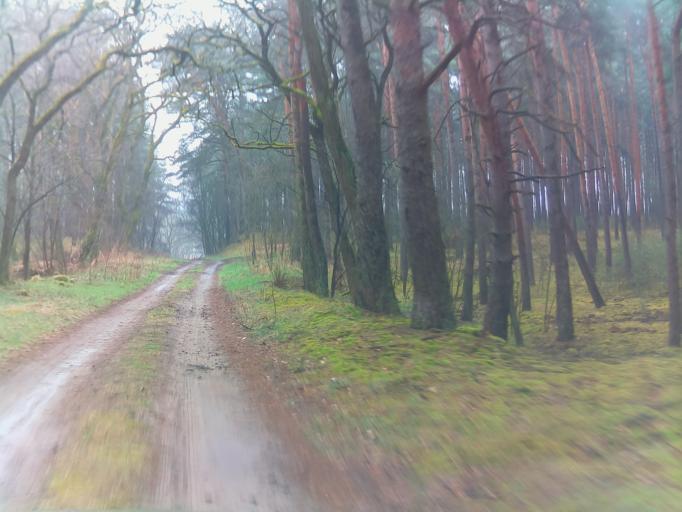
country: DE
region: Brandenburg
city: Jamlitz
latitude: 52.0429
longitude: 14.3651
